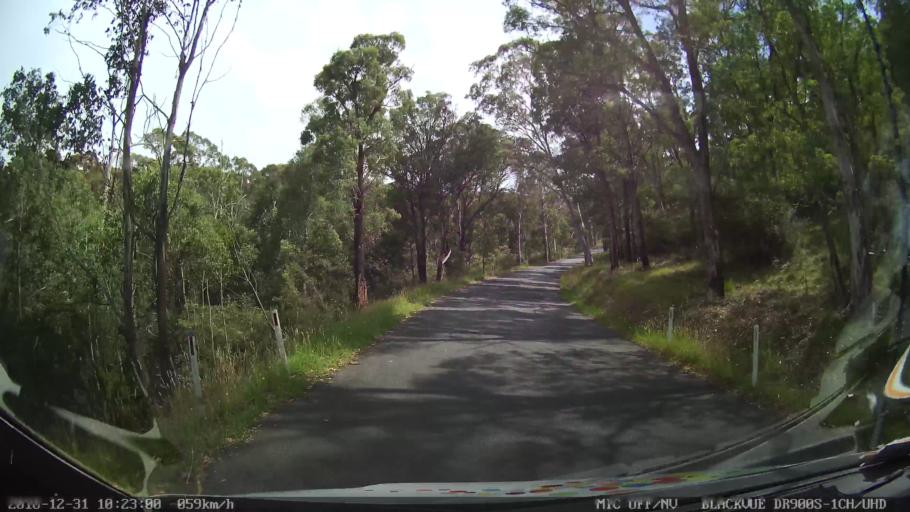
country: AU
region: New South Wales
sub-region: Snowy River
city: Jindabyne
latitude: -36.5207
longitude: 148.1431
